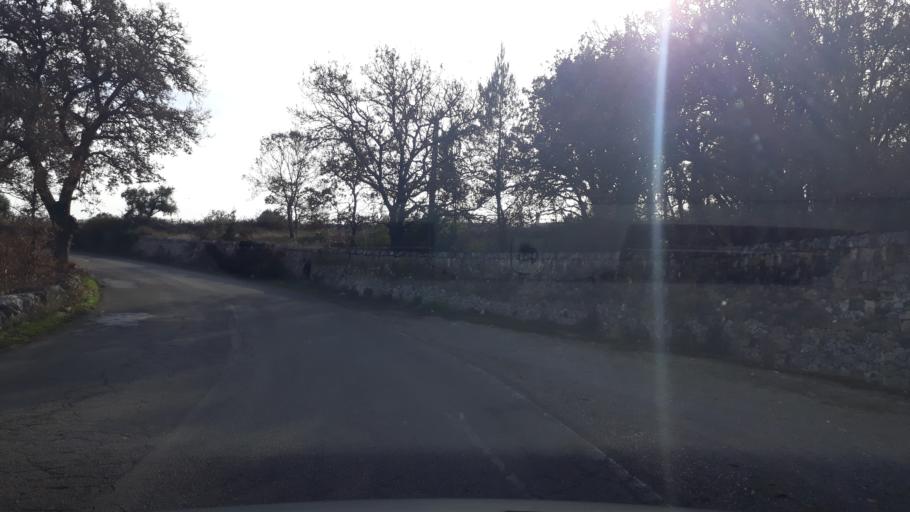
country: IT
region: Apulia
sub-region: Provincia di Taranto
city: Martina Franca
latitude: 40.6769
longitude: 17.3590
